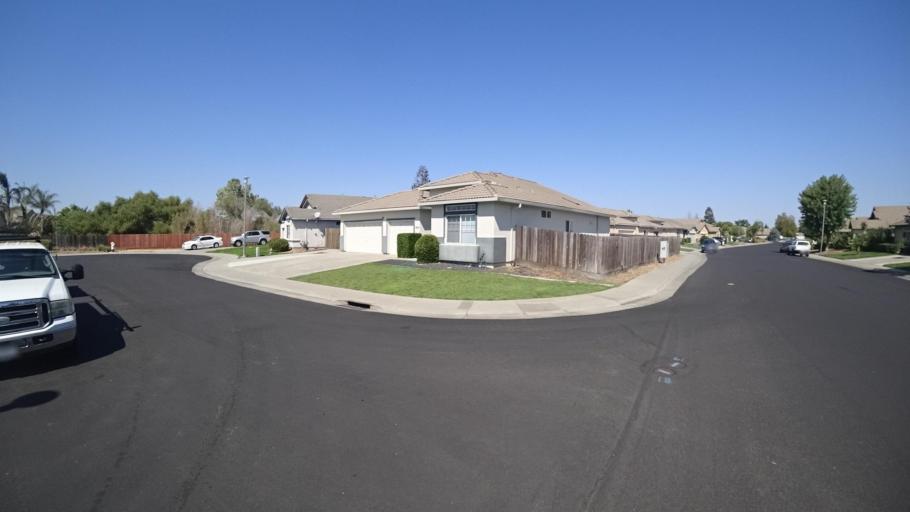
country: US
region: California
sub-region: Sacramento County
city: Elk Grove
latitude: 38.4484
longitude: -121.3897
